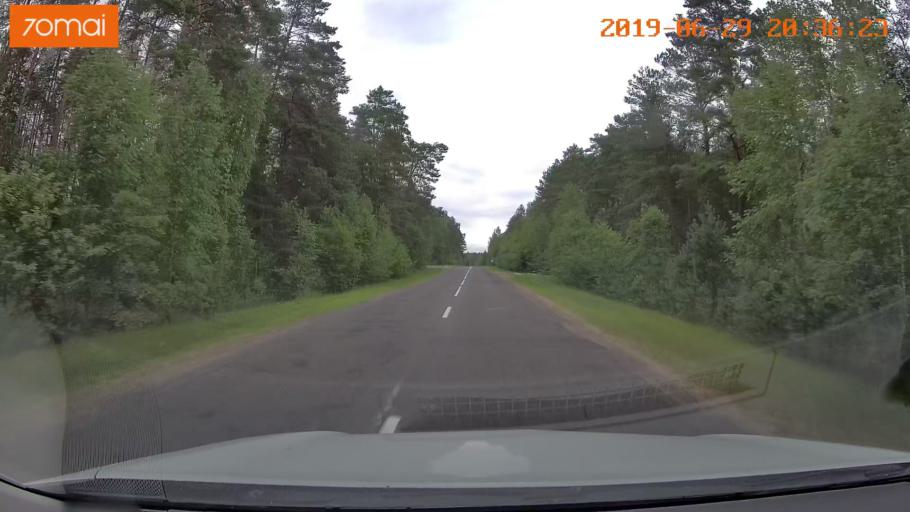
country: BY
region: Brest
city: Hantsavichy
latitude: 52.5257
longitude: 26.3581
